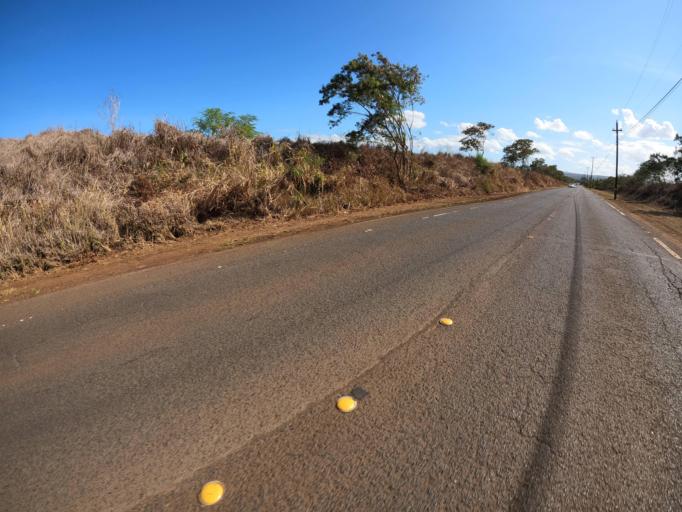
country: US
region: Hawaii
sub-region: Honolulu County
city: Waialua
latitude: 21.5700
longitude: -158.1379
